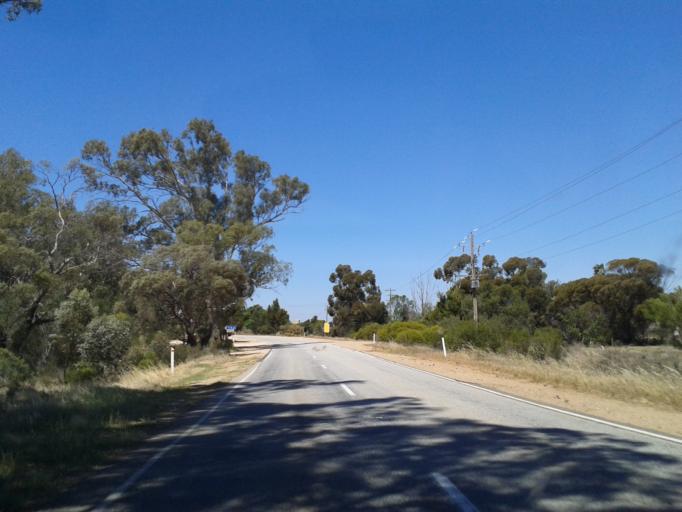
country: AU
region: Victoria
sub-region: Swan Hill
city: Swan Hill
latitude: -34.7181
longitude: 143.1647
